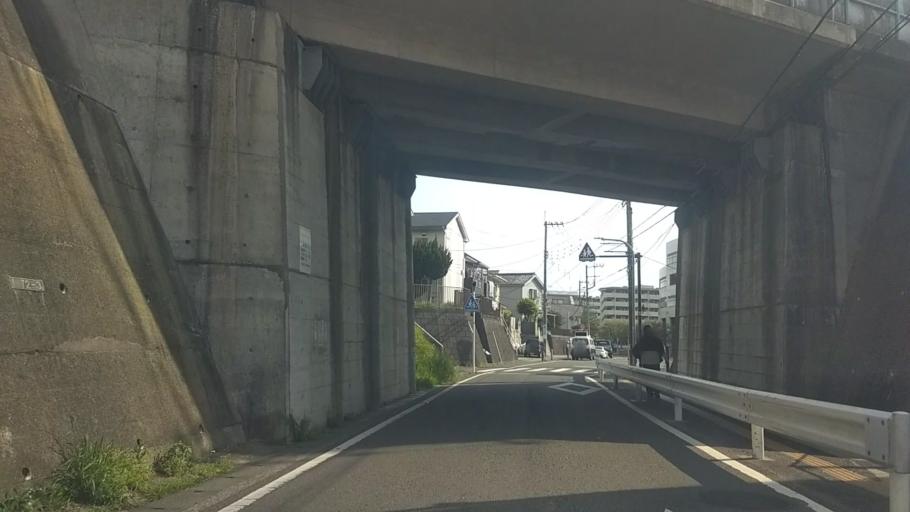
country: JP
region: Kanagawa
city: Kamakura
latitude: 35.3692
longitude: 139.5545
